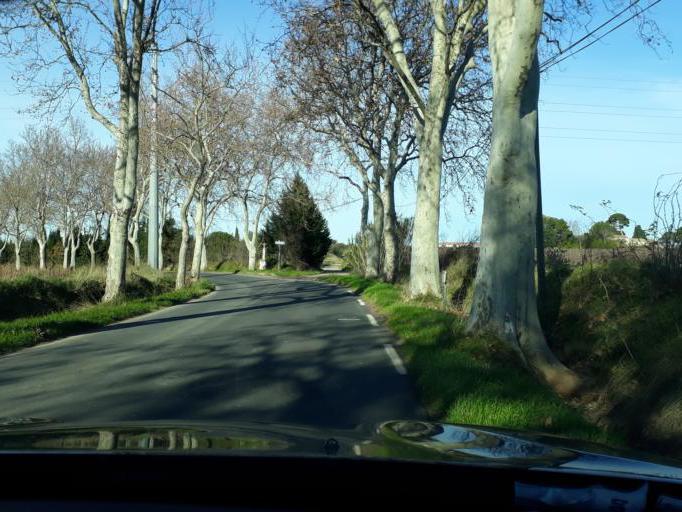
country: FR
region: Languedoc-Roussillon
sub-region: Departement de l'Herault
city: Florensac
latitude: 43.3931
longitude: 3.4594
